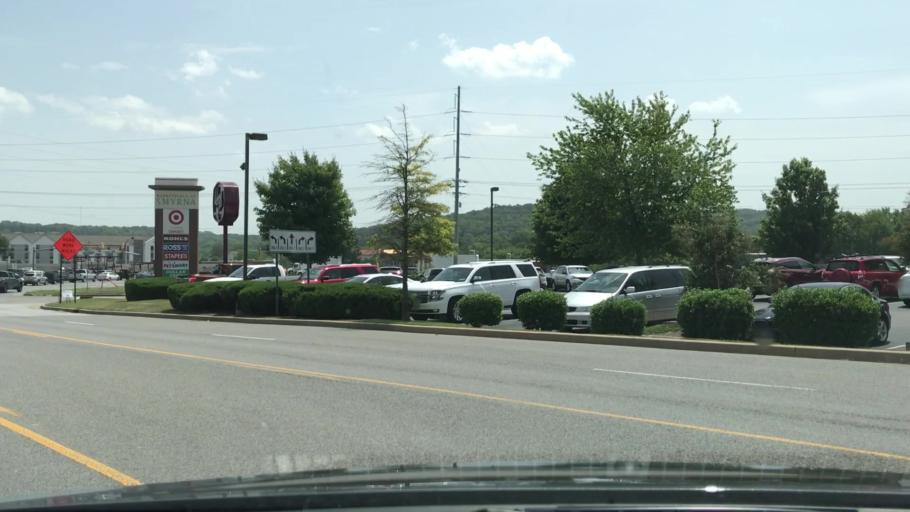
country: US
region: Tennessee
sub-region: Rutherford County
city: La Vergne
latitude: 35.9791
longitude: -86.5648
